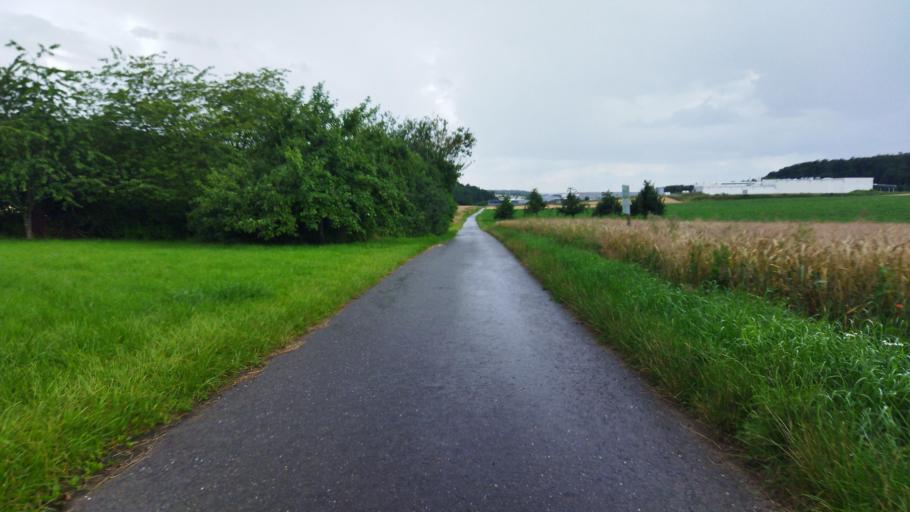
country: DE
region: Baden-Wuerttemberg
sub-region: Regierungsbezirk Stuttgart
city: Kirchardt
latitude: 49.2019
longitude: 9.0196
